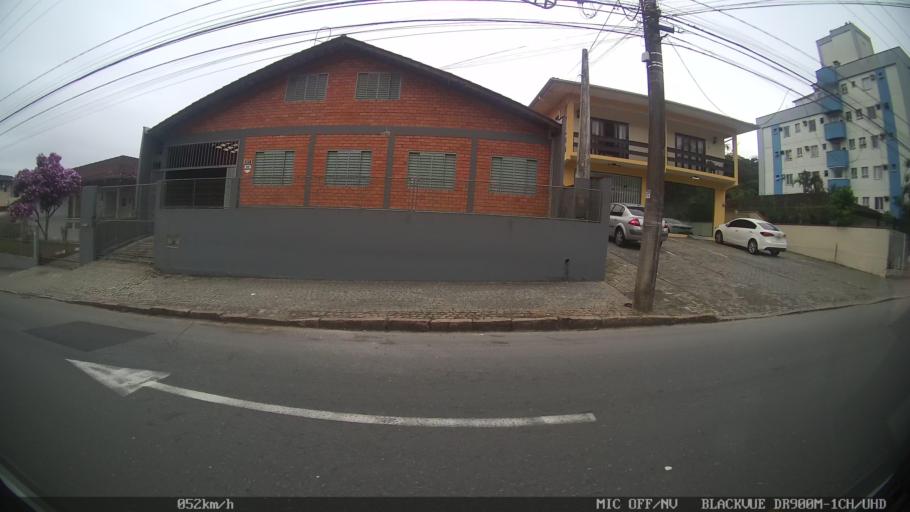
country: BR
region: Santa Catarina
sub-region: Joinville
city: Joinville
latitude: -26.2691
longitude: -48.8349
